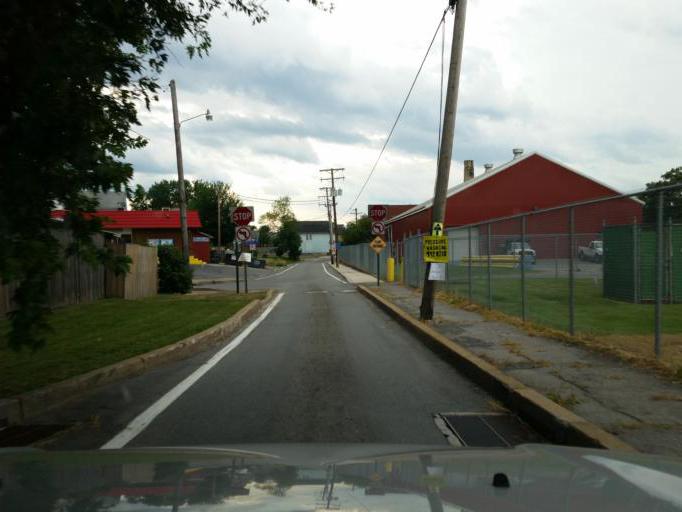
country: US
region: Pennsylvania
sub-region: Blair County
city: Altoona
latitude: 40.5243
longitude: -78.3860
